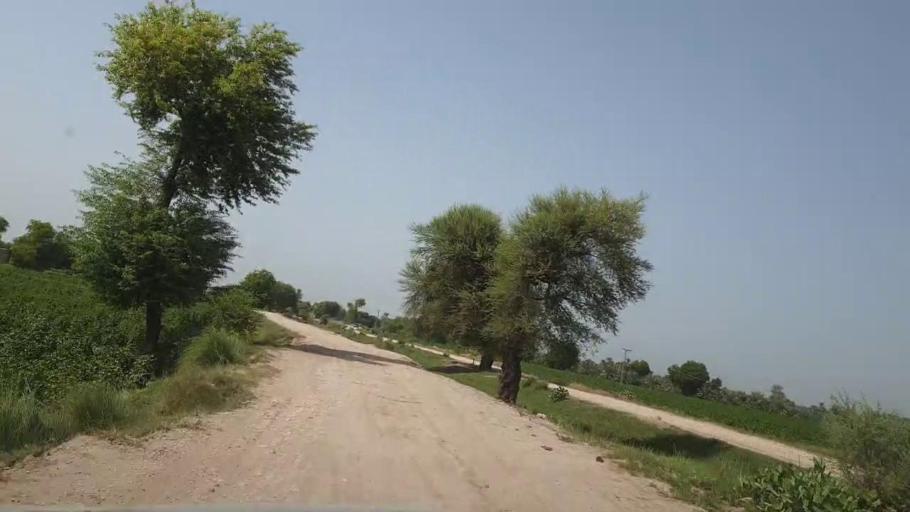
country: PK
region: Sindh
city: Pano Aqil
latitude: 27.8352
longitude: 69.1853
